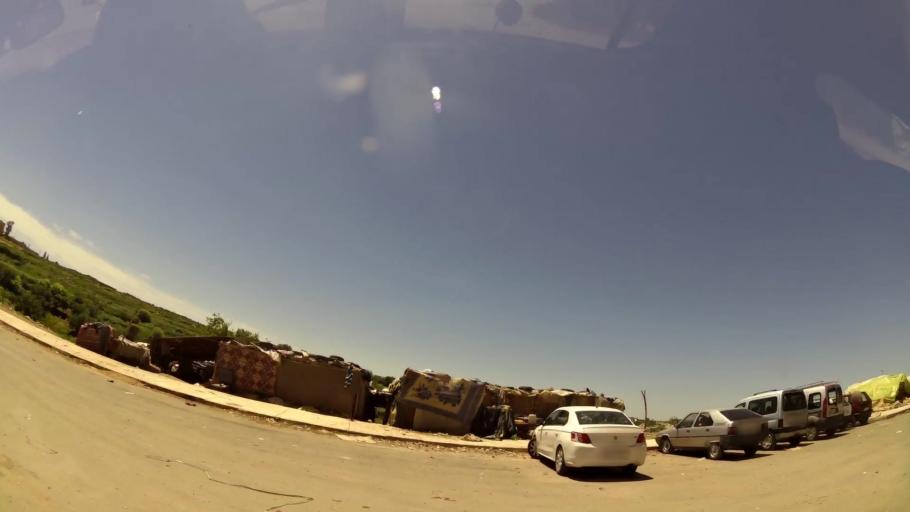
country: MA
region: Meknes-Tafilalet
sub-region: Meknes
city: Meknes
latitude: 33.9071
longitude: -5.5805
